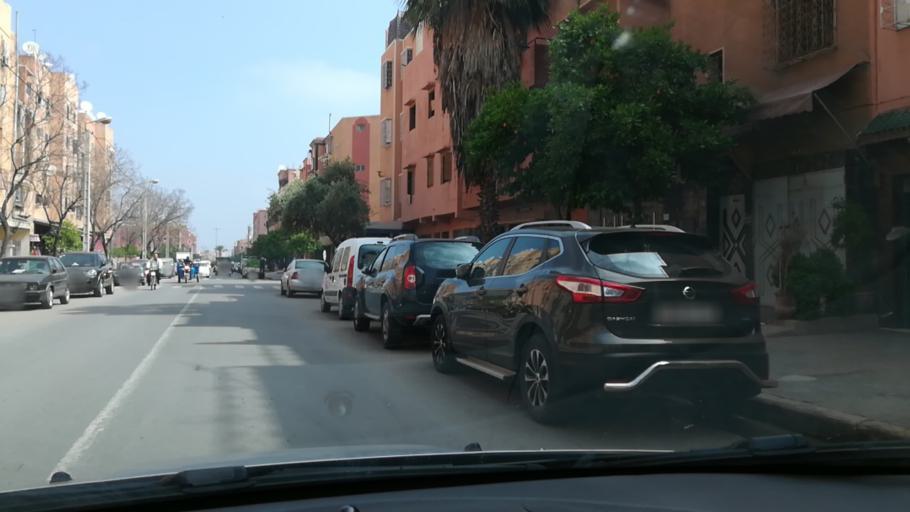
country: MA
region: Marrakech-Tensift-Al Haouz
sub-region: Marrakech
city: Marrakesh
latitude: 31.6321
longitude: -8.0624
